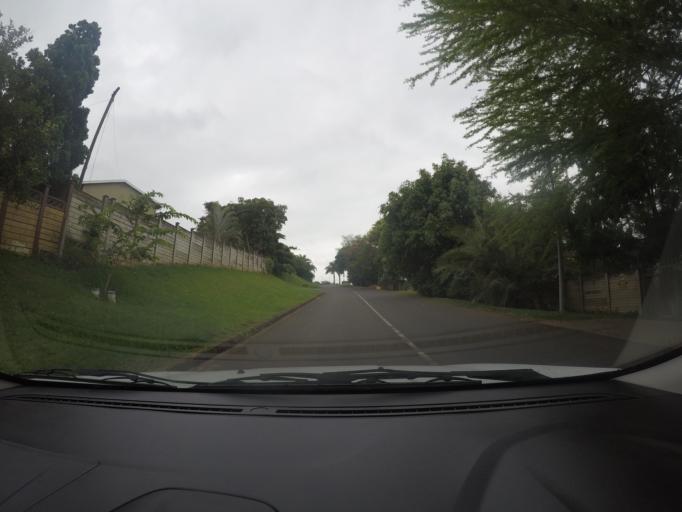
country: ZA
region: KwaZulu-Natal
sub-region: uThungulu District Municipality
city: Empangeni
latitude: -28.7631
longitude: 31.8869
